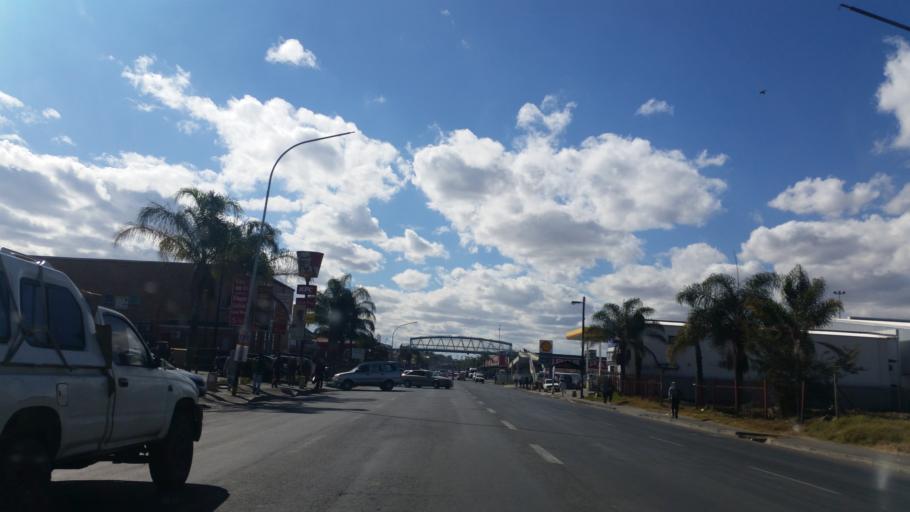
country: ZA
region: KwaZulu-Natal
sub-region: uThukela District Municipality
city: Ladysmith
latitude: -28.5623
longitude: 29.7817
